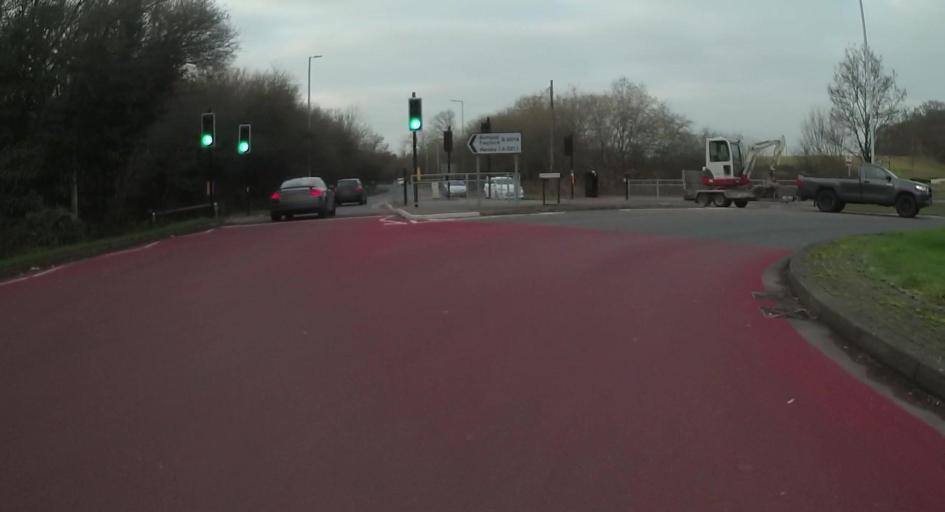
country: GB
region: England
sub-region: Bracknell Forest
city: Bracknell
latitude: 51.4269
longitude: -0.7660
